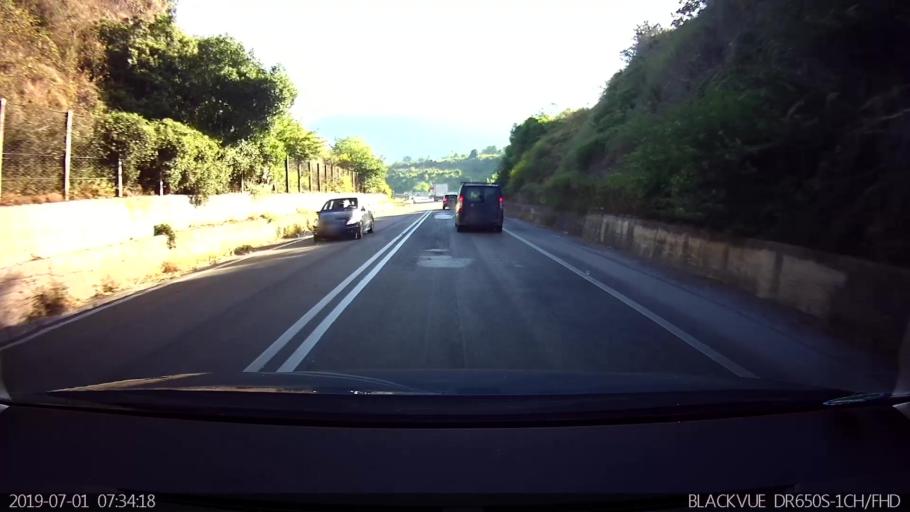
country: IT
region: Latium
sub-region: Provincia di Latina
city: Prossedi
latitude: 41.5145
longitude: 13.2706
